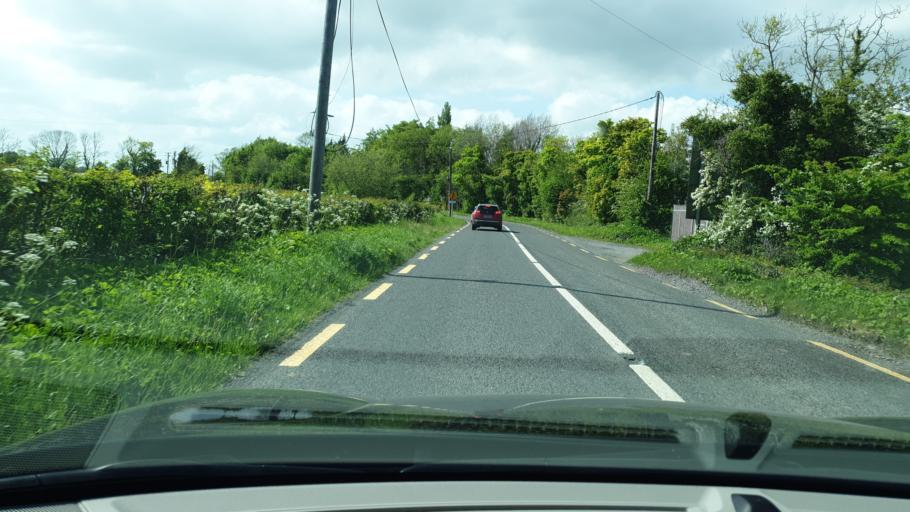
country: IE
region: Leinster
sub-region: An Mhi
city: Ratoath
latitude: 53.5159
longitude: -6.4894
